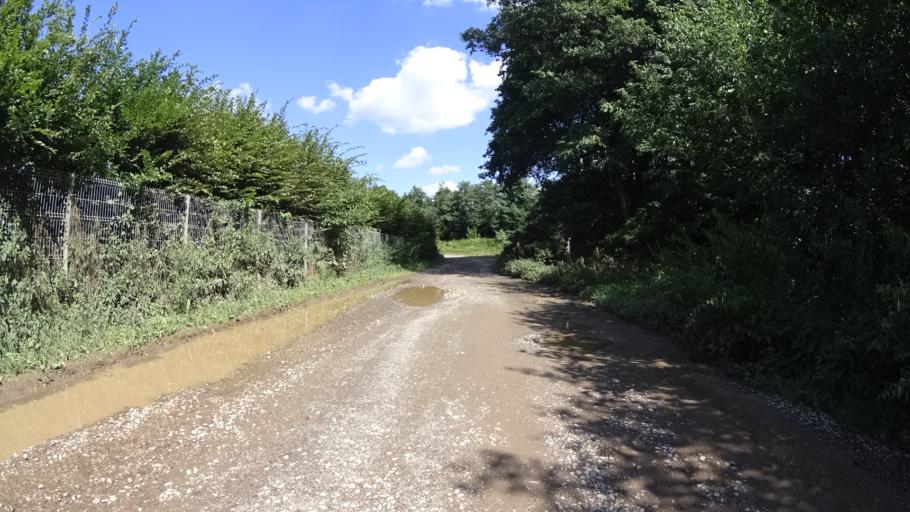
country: PL
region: Masovian Voivodeship
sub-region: Powiat grojecki
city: Mogielnica
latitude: 51.6699
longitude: 20.7445
